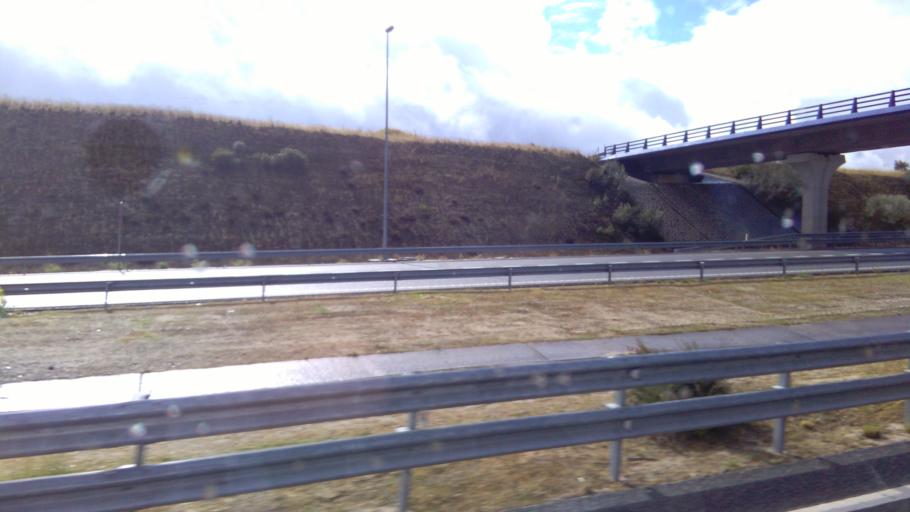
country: ES
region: Madrid
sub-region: Provincia de Madrid
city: El Alamo
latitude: 40.2600
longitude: -3.9805
